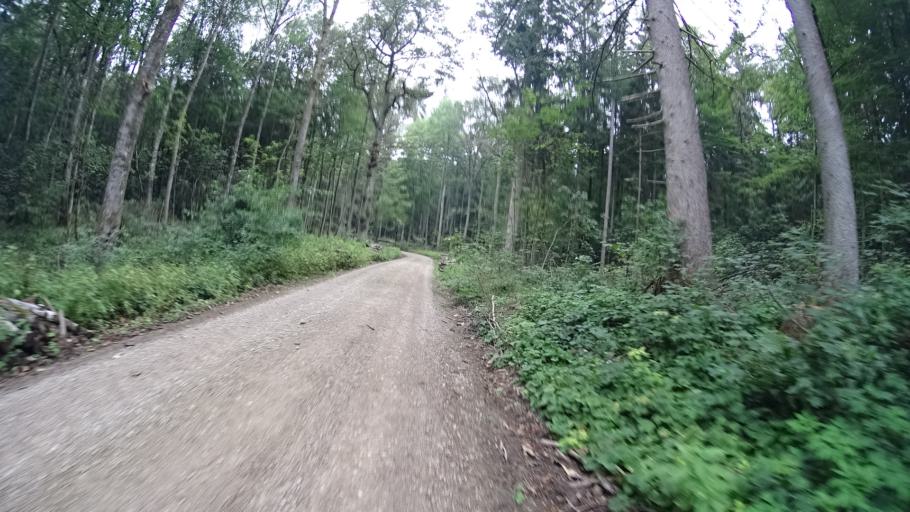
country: DE
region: Bavaria
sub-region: Upper Bavaria
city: Stammham
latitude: 48.8503
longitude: 11.4943
